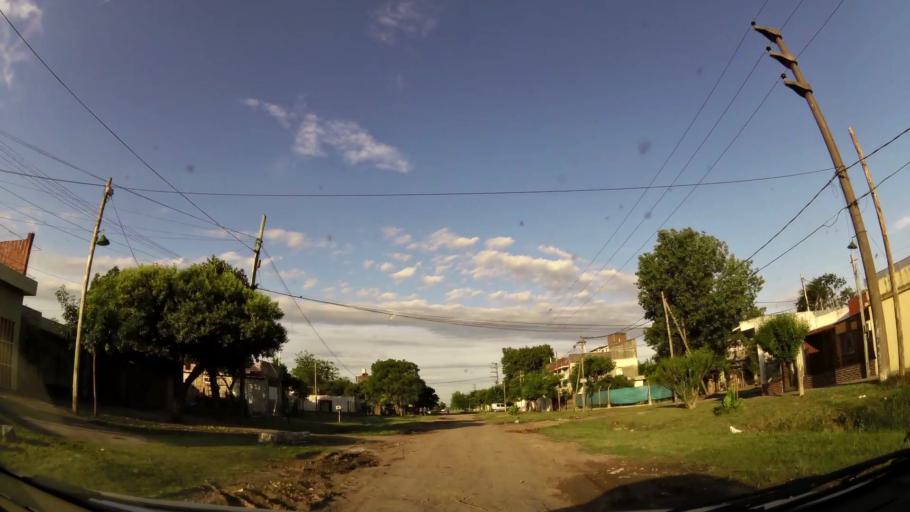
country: AR
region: Buenos Aires
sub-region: Partido de Merlo
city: Merlo
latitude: -34.6930
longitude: -58.7486
